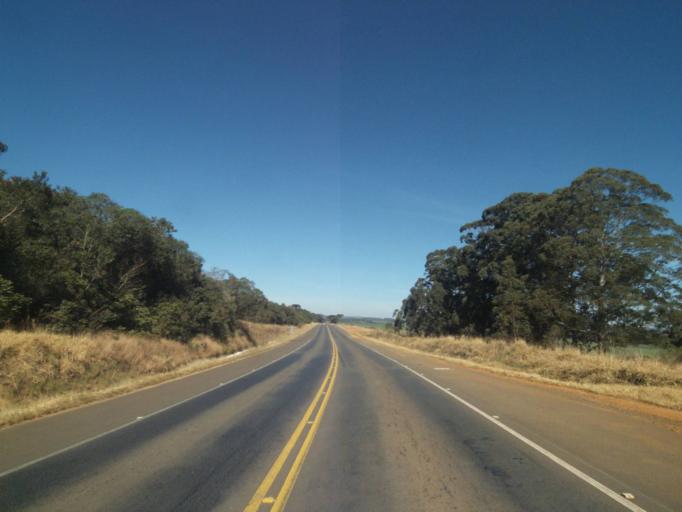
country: BR
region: Parana
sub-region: Tibagi
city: Tibagi
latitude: -24.6970
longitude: -50.4457
